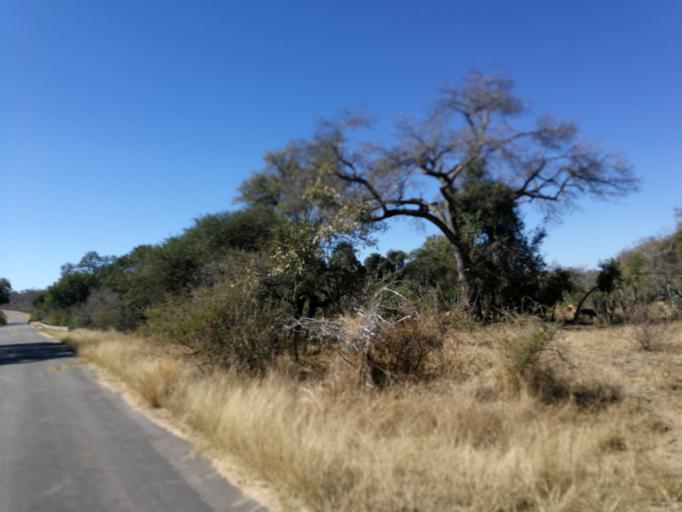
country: ZA
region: Limpopo
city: Thulamahashi
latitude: -24.9427
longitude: 31.6767
